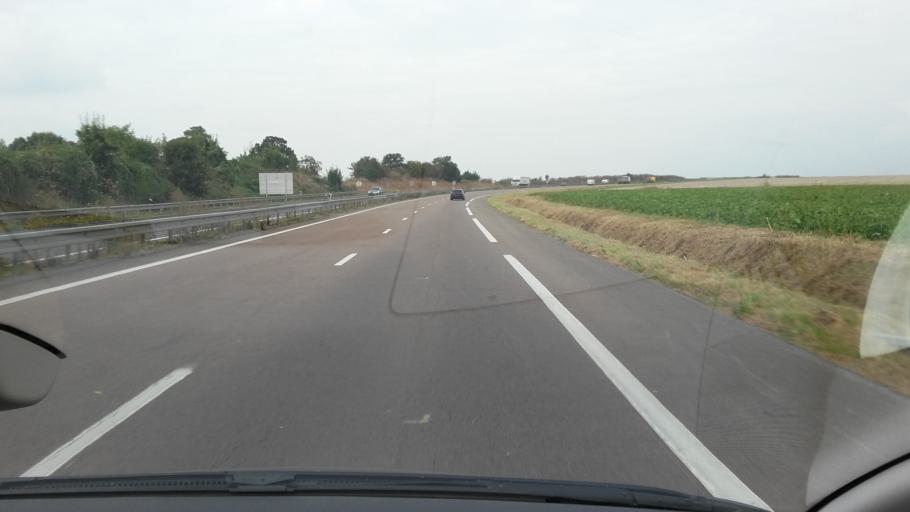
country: FR
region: Champagne-Ardenne
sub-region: Departement de la Marne
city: Warmeriville
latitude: 49.3609
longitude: 4.2081
